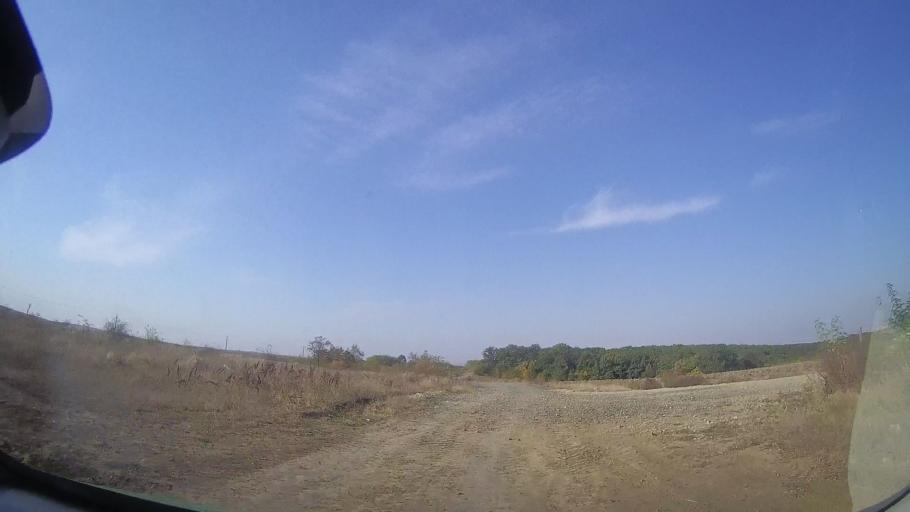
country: RO
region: Timis
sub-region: Oras Recas
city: Recas
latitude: 45.8784
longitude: 21.5302
